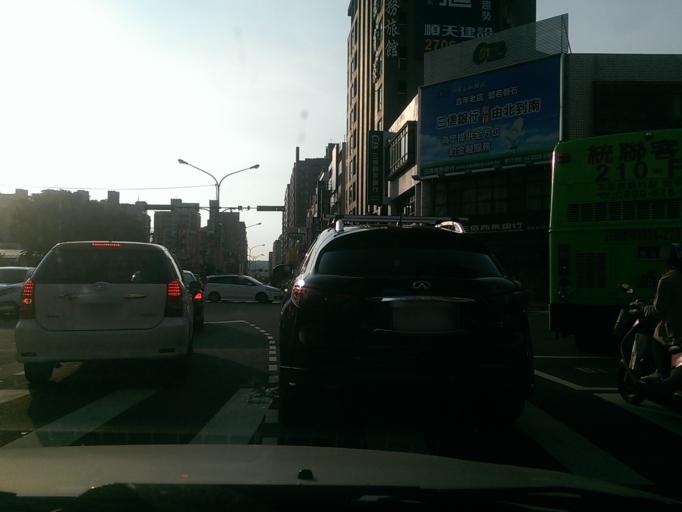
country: TW
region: Taiwan
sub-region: Taichung City
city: Taichung
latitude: 24.1713
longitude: 120.6445
